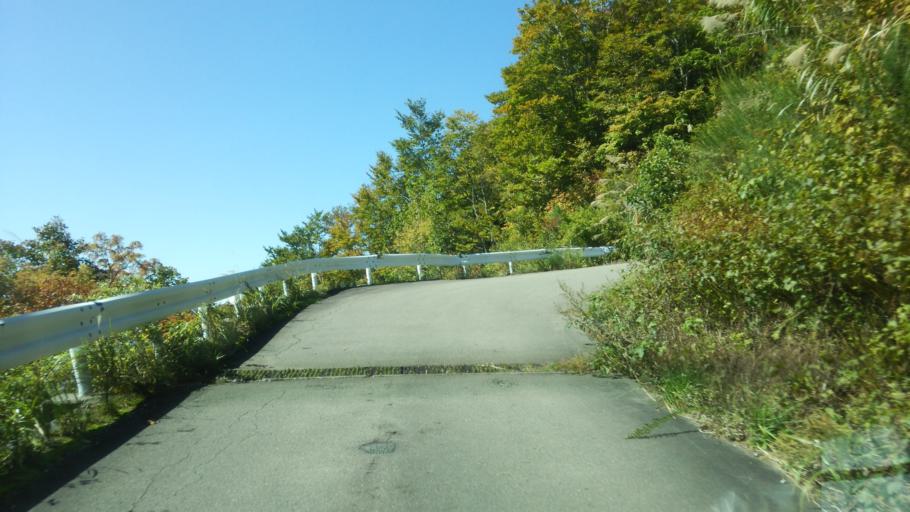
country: JP
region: Fukushima
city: Kitakata
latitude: 37.6213
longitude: 139.9890
